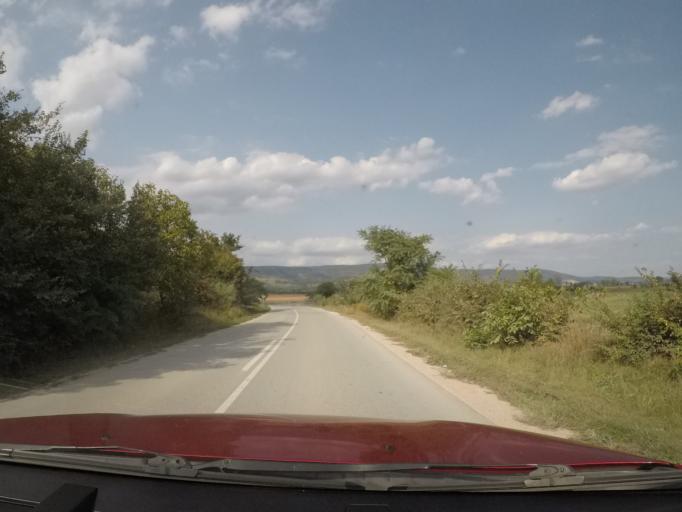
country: SK
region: Kosicky
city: Medzev
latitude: 48.5863
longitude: 20.8530
